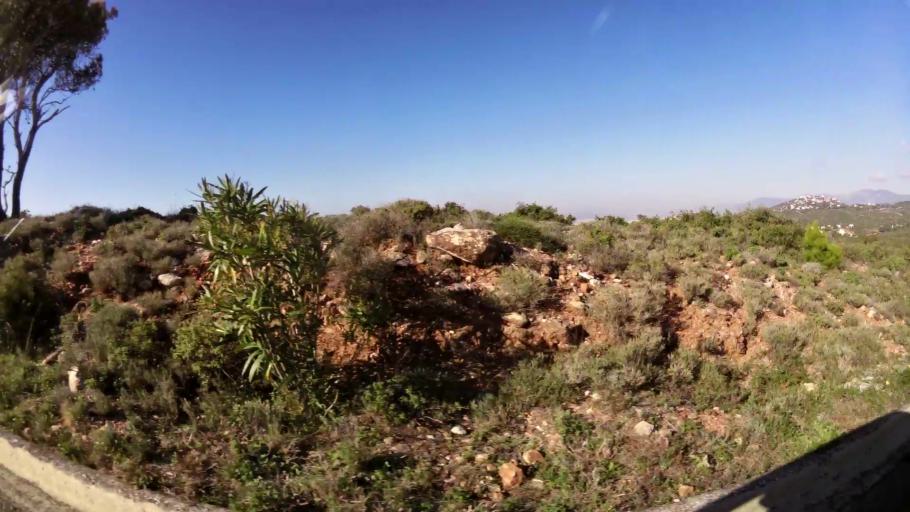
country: GR
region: Attica
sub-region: Nomarchia Anatolikis Attikis
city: Dhrafi
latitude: 38.0307
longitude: 23.8925
